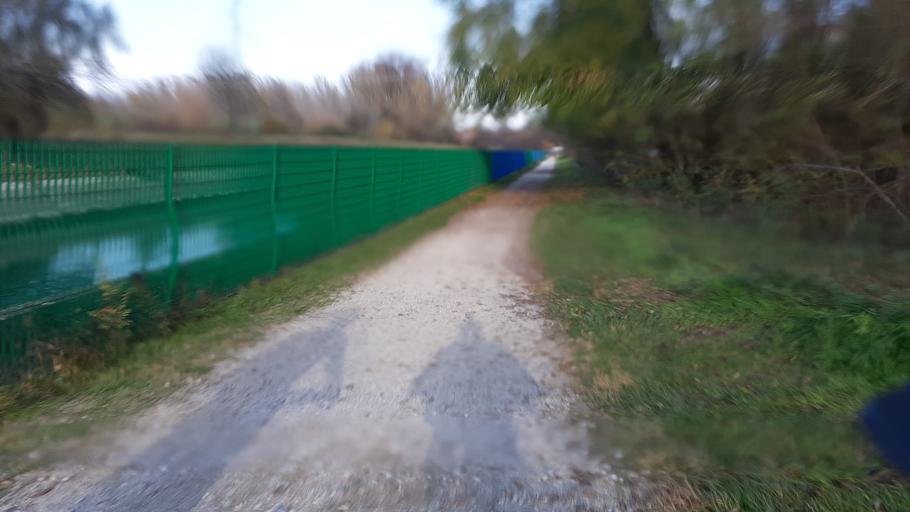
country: IT
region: Piedmont
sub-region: Provincia di Torino
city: San Mauro Torinese
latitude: 45.1083
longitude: 7.7703
